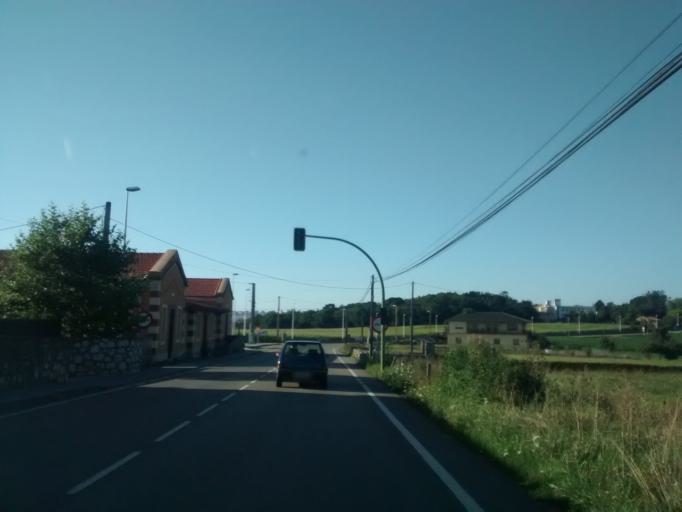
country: ES
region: Cantabria
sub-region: Provincia de Cantabria
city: Santander
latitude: 43.4305
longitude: -3.7725
